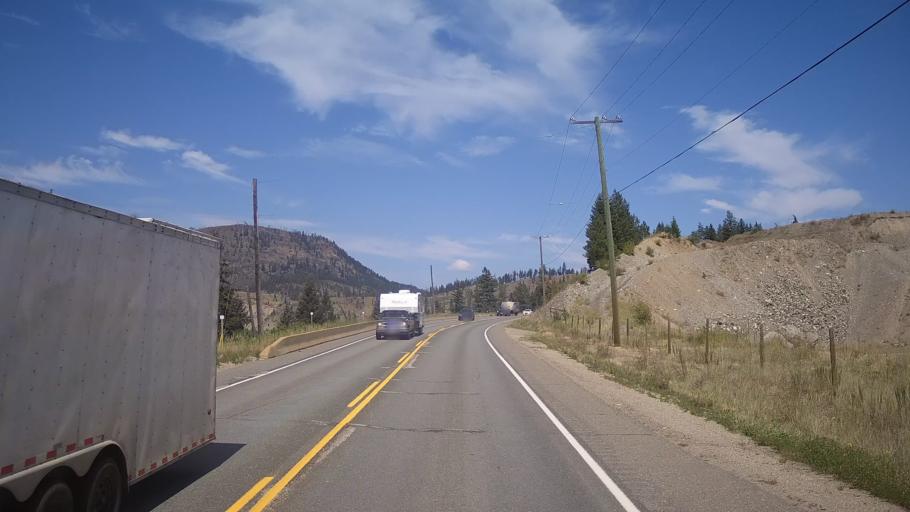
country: CA
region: British Columbia
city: Kamloops
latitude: 51.0731
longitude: -120.2087
